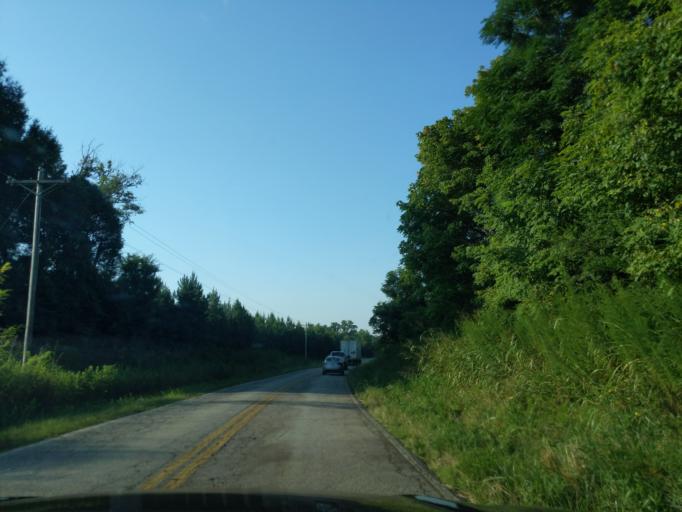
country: US
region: South Carolina
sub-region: Spartanburg County
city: Roebuck
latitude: 34.7956
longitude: -81.9728
